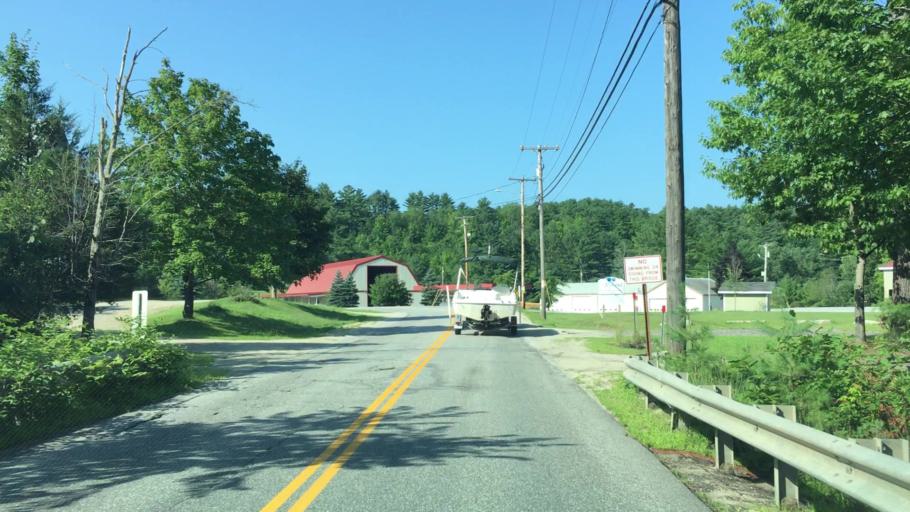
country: US
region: Maine
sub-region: Androscoggin County
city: Poland
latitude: 44.0619
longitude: -70.3889
